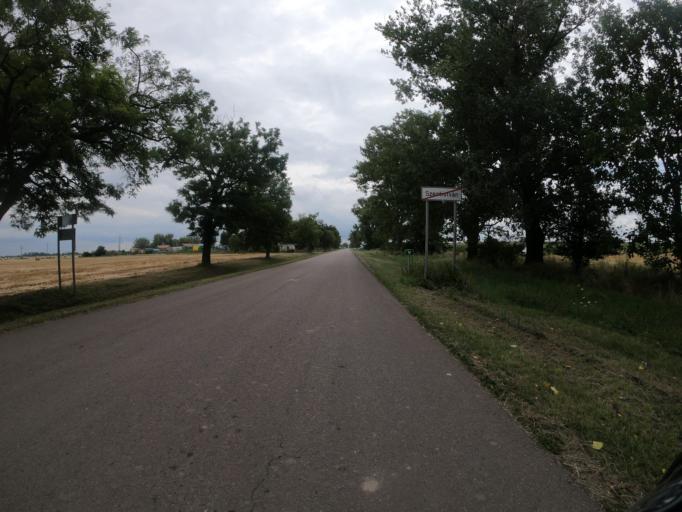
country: HU
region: Borsod-Abauj-Zemplen
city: Szentistvan
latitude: 47.7677
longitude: 20.6700
